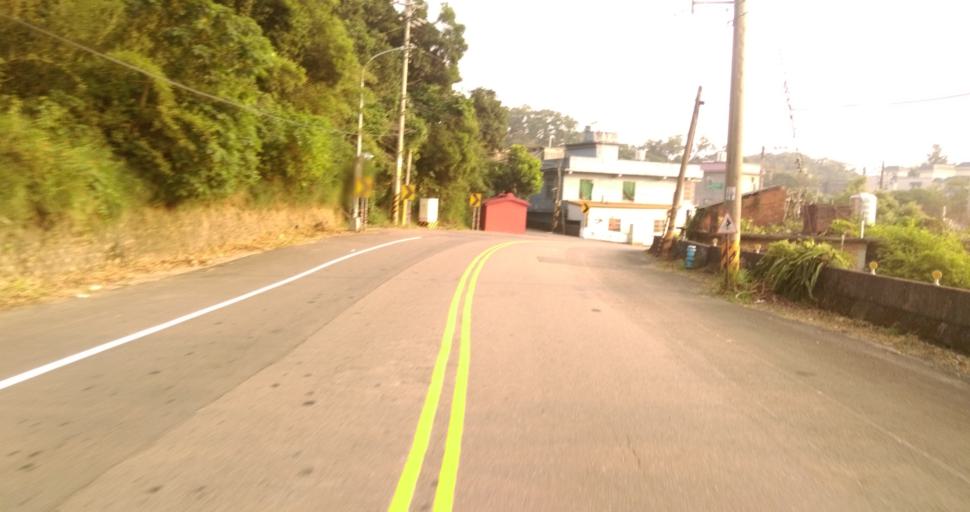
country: TW
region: Taiwan
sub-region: Hsinchu
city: Hsinchu
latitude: 24.7484
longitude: 120.9376
